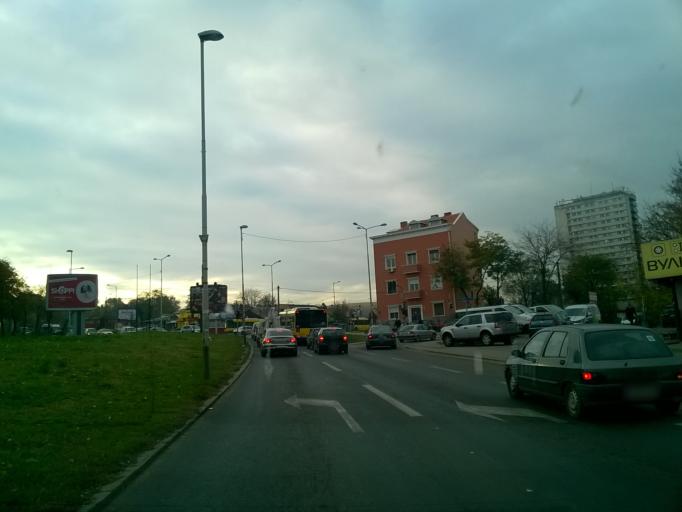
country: RS
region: Central Serbia
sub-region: Belgrade
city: Palilula
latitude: 44.8163
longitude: 20.4896
